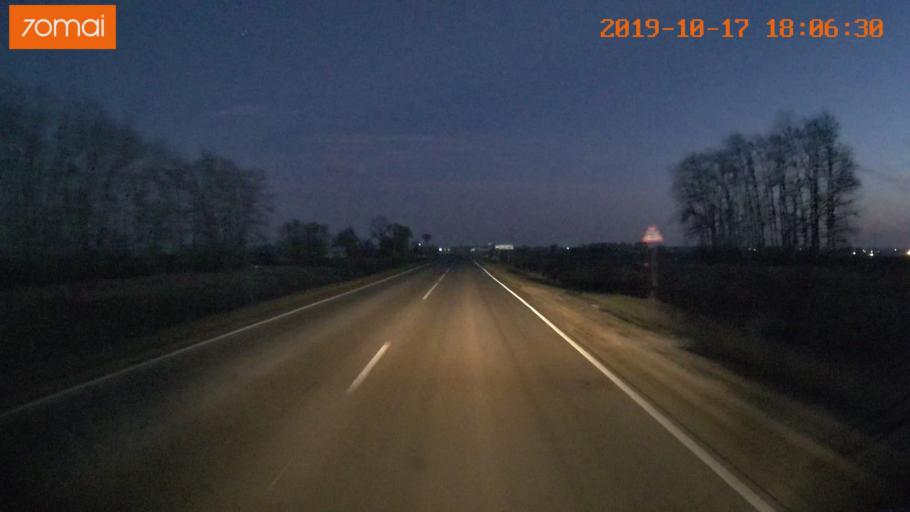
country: RU
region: Tula
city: Kurkino
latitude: 53.4499
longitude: 38.6576
